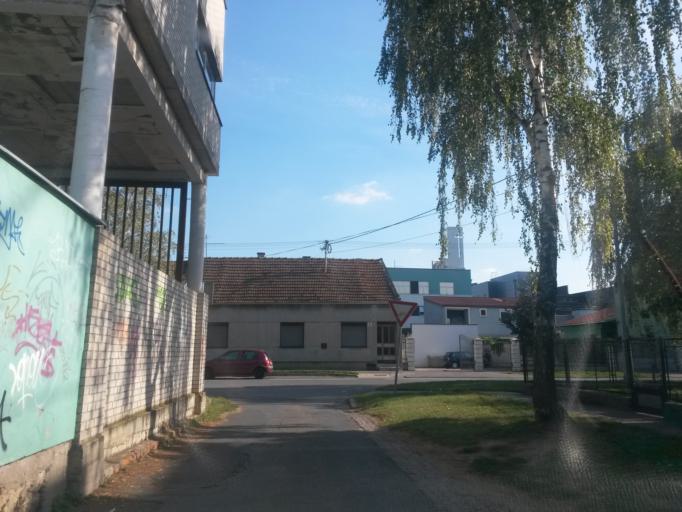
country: HR
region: Osjecko-Baranjska
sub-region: Grad Osijek
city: Osijek
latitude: 45.5516
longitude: 18.7048
